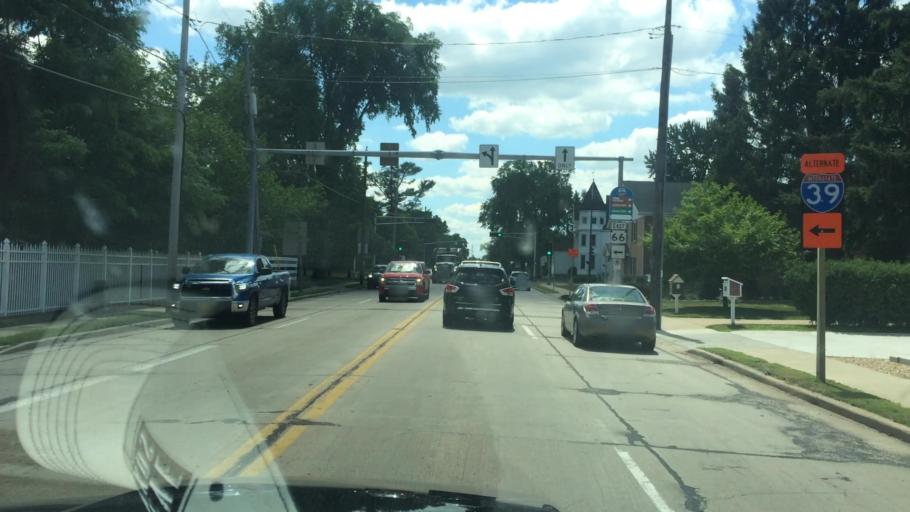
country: US
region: Wisconsin
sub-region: Portage County
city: Stevens Point
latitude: 44.5233
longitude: -89.5749
